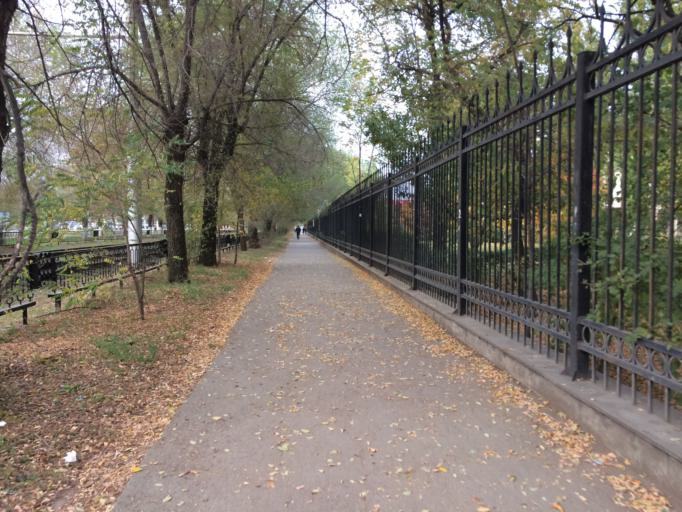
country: RU
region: Volgograd
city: Krasnoslobodsk
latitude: 48.7377
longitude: 44.5461
